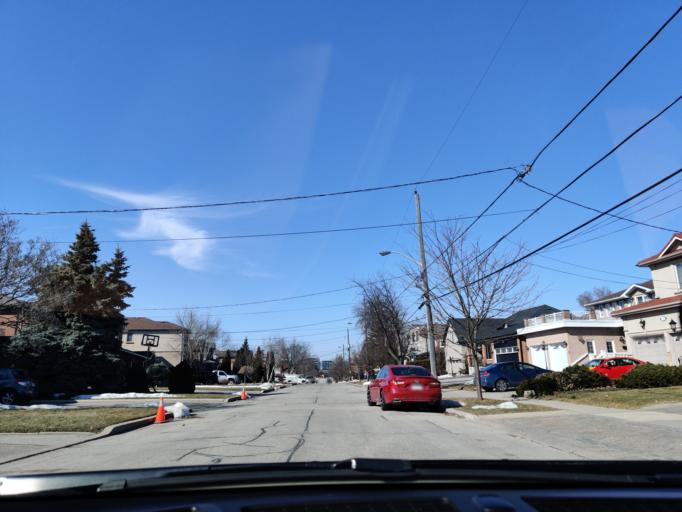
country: CA
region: Ontario
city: Toronto
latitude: 43.7166
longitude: -79.4771
